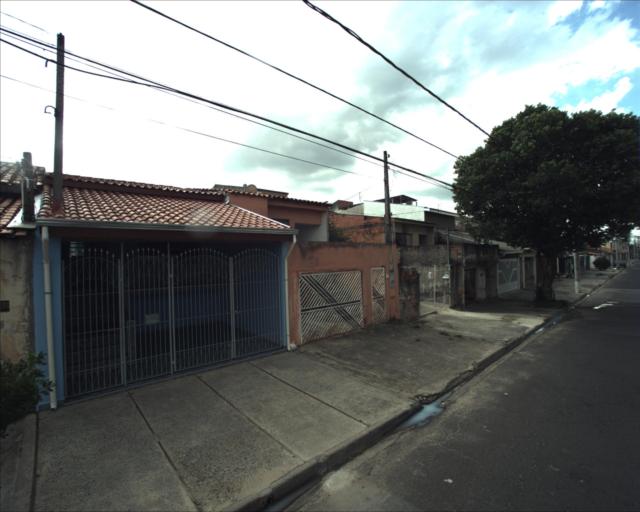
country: BR
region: Sao Paulo
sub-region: Sorocaba
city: Sorocaba
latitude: -23.4634
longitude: -47.4704
